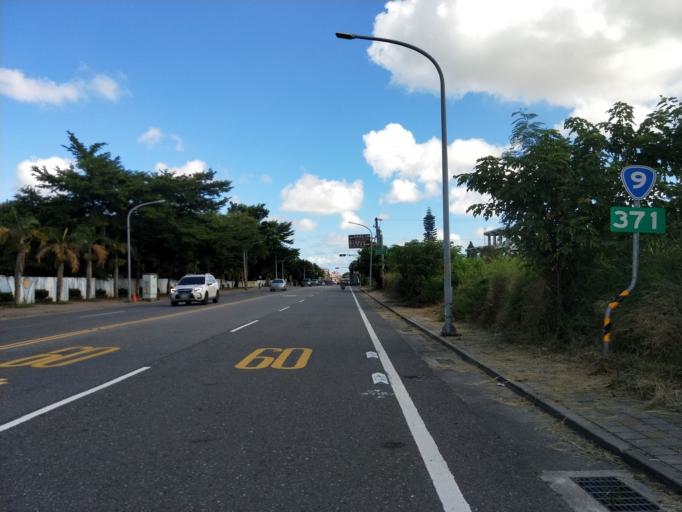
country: TW
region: Taiwan
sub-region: Taitung
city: Taitung
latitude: 22.7890
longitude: 121.1110
